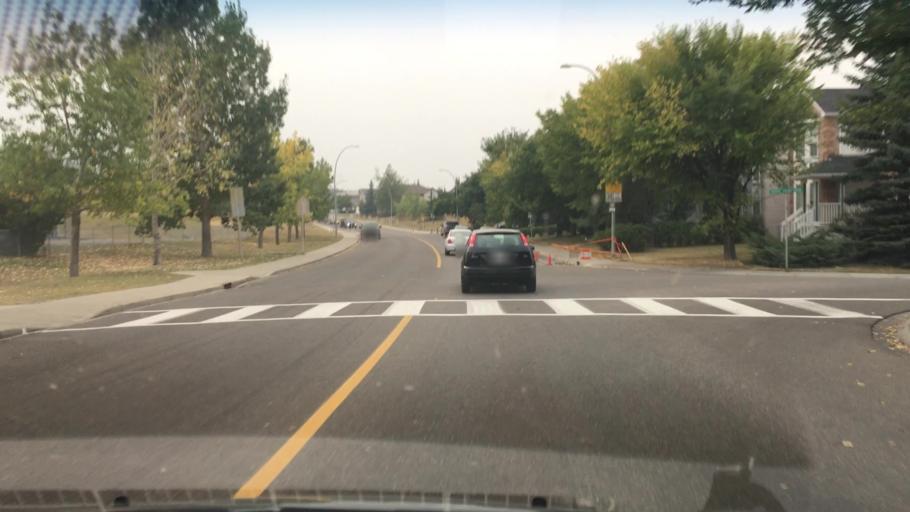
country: CA
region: Alberta
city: Calgary
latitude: 51.1516
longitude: -114.1112
